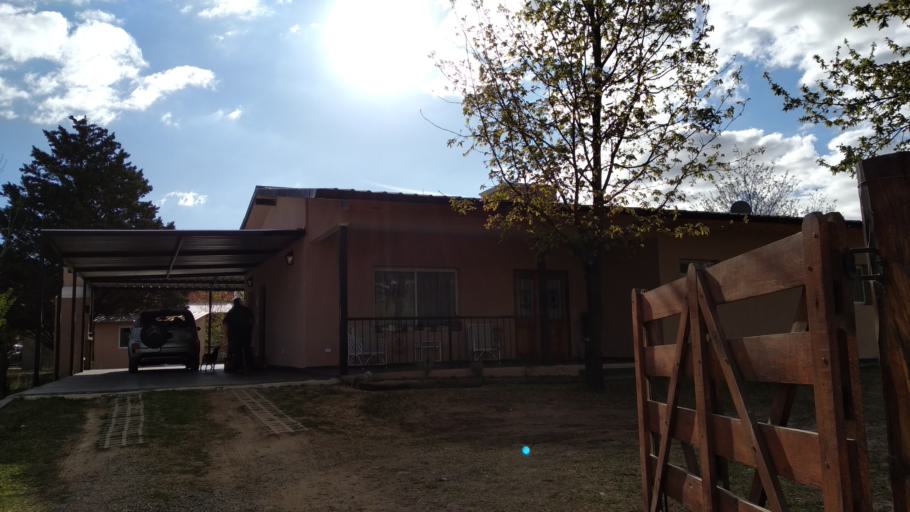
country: AR
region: Cordoba
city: Mina Clavero
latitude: -31.7289
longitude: -65.0255
